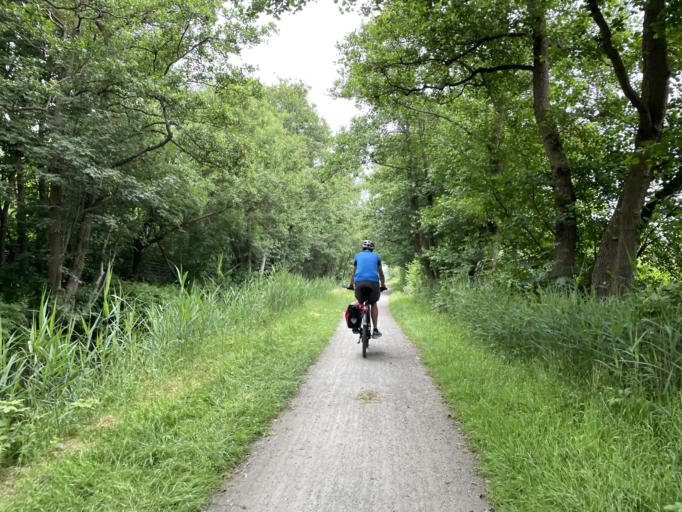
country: DE
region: Lower Saxony
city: Cuxhaven
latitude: 53.8662
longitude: 8.6597
